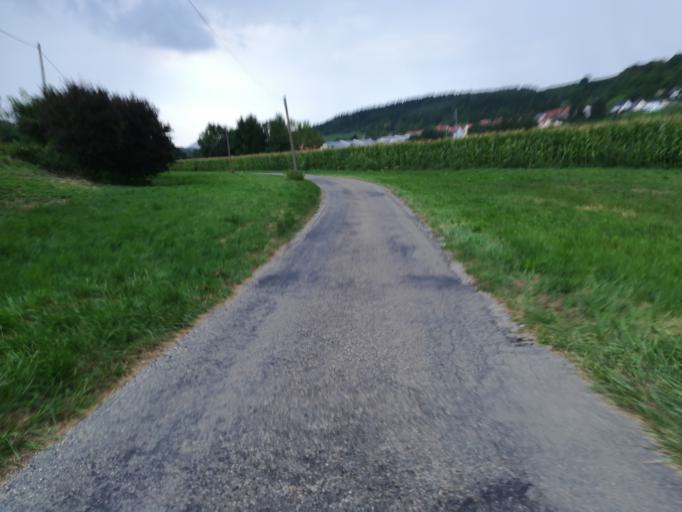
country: DE
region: Baden-Wuerttemberg
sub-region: Freiburg Region
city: Hilzingen
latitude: 47.7570
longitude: 8.8067
